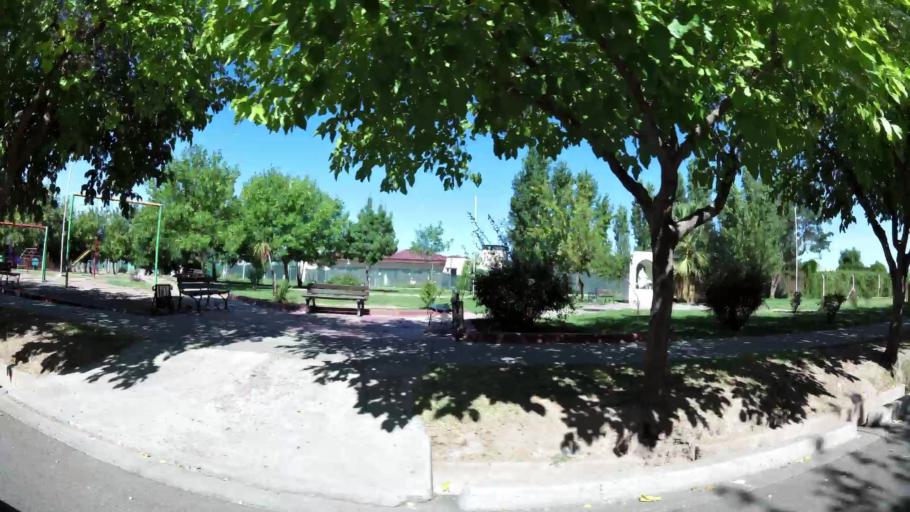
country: AR
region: Mendoza
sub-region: Departamento de Godoy Cruz
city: Godoy Cruz
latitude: -32.9481
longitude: -68.8123
